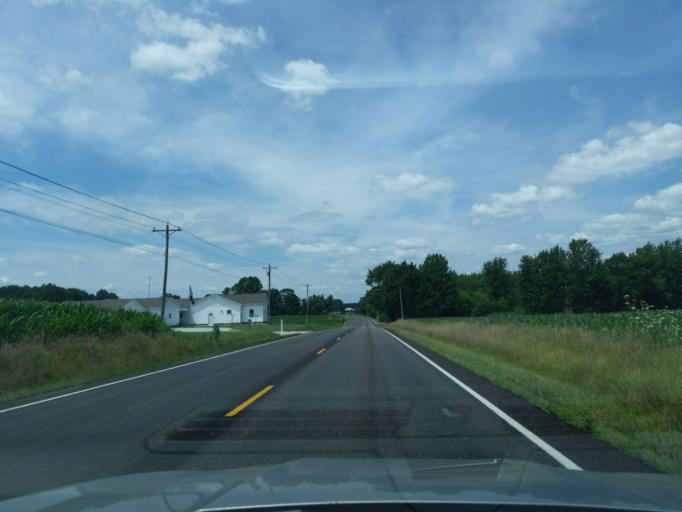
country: US
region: Indiana
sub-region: Ripley County
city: Osgood
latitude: 39.2398
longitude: -85.3448
